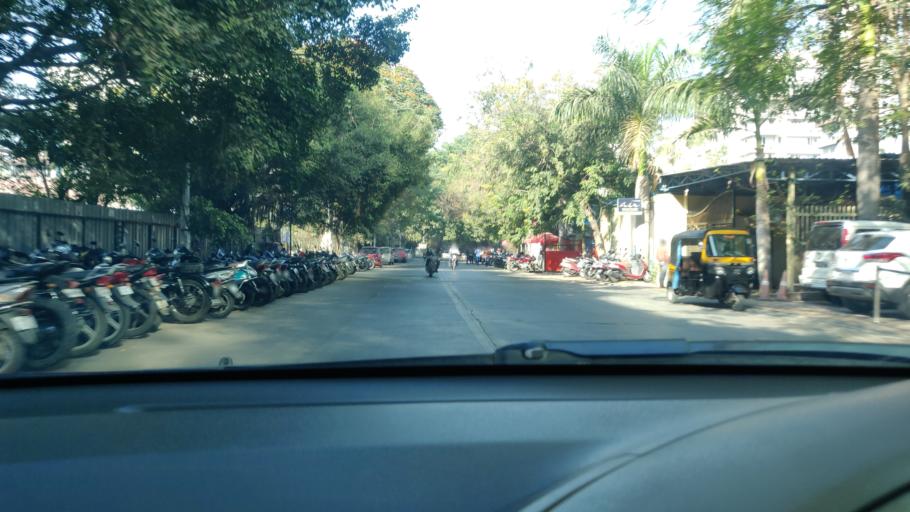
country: IN
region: Maharashtra
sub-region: Pune Division
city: Khadki
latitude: 18.5536
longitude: 73.8067
